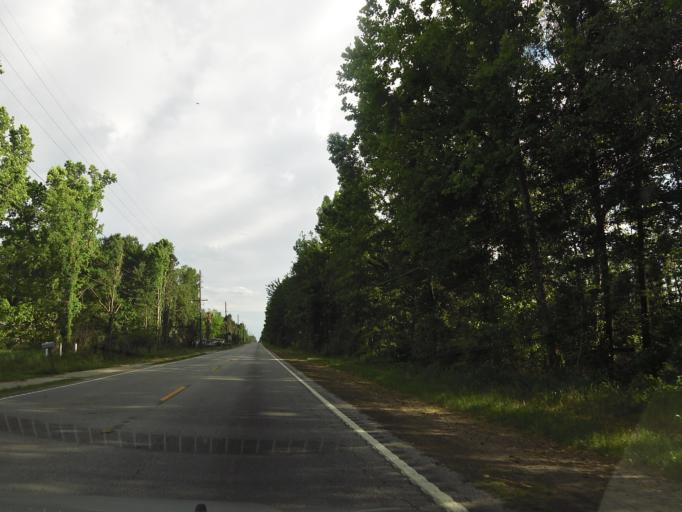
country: US
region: South Carolina
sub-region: Hampton County
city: Estill
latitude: 32.7377
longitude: -81.2417
